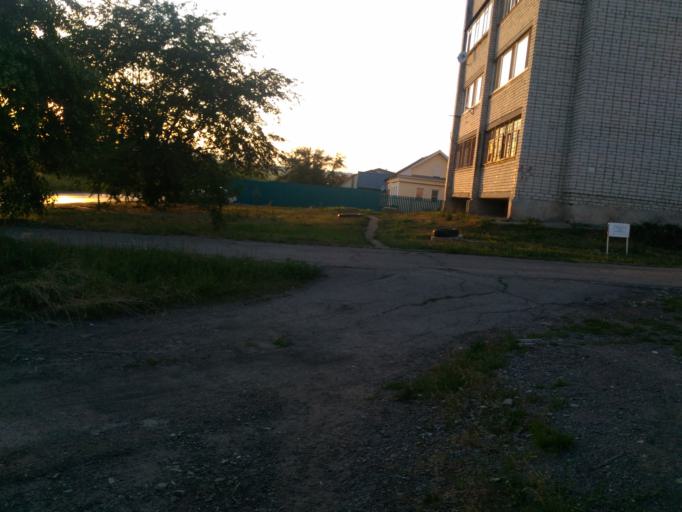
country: RU
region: Ulyanovsk
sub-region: Ulyanovskiy Rayon
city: Ulyanovsk
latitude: 54.3357
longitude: 48.3638
